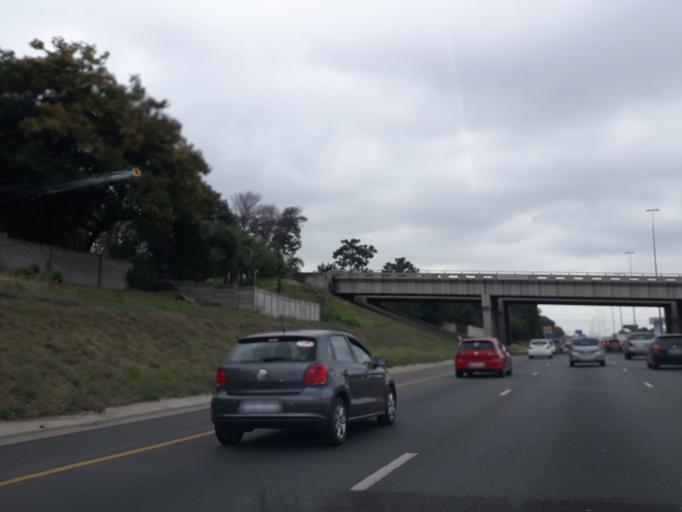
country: ZA
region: Gauteng
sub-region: City of Johannesburg Metropolitan Municipality
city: Roodepoort
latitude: -26.0927
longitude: 27.9673
